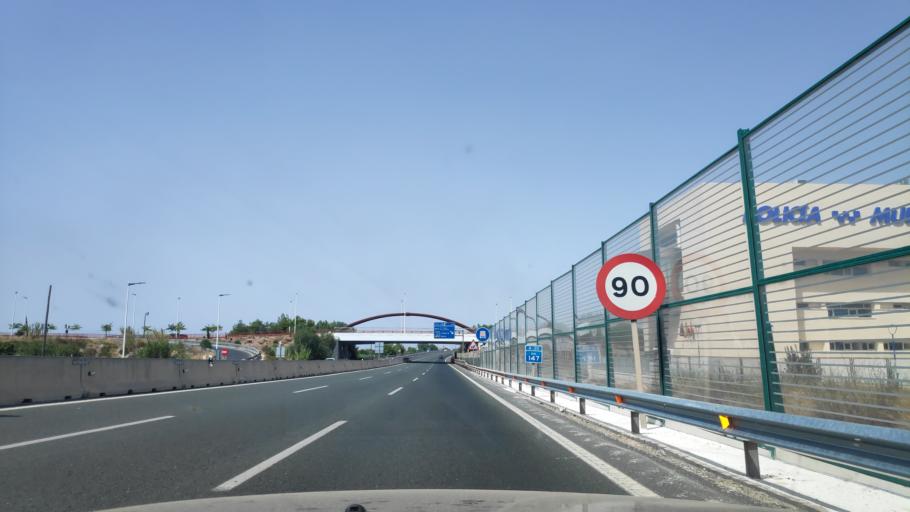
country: ES
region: Murcia
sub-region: Murcia
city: Murcia
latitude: 37.9415
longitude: -1.1500
